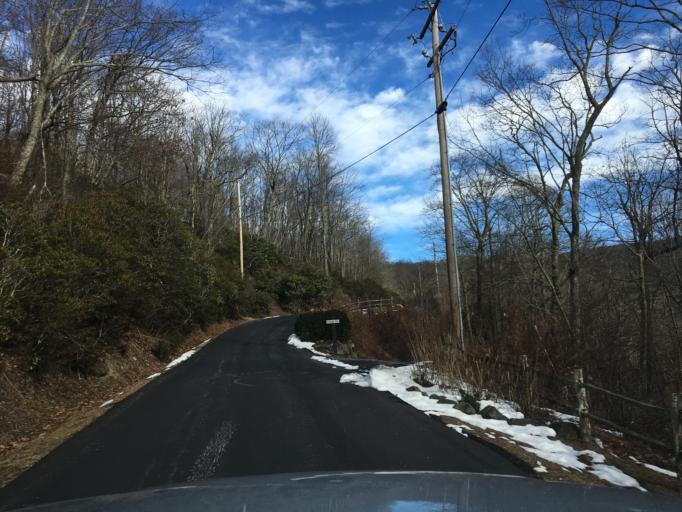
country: US
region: North Carolina
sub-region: Jackson County
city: Cullowhee
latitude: 35.1343
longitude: -83.0001
